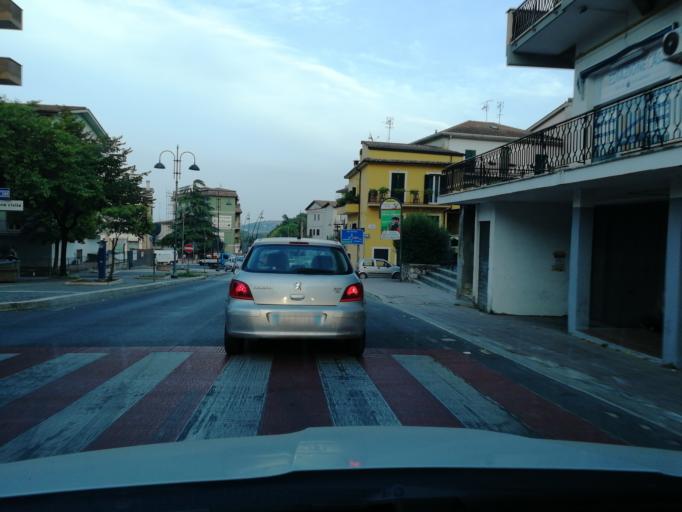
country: IT
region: Latium
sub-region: Citta metropolitana di Roma Capitale
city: Artena
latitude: 41.7420
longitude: 12.9135
